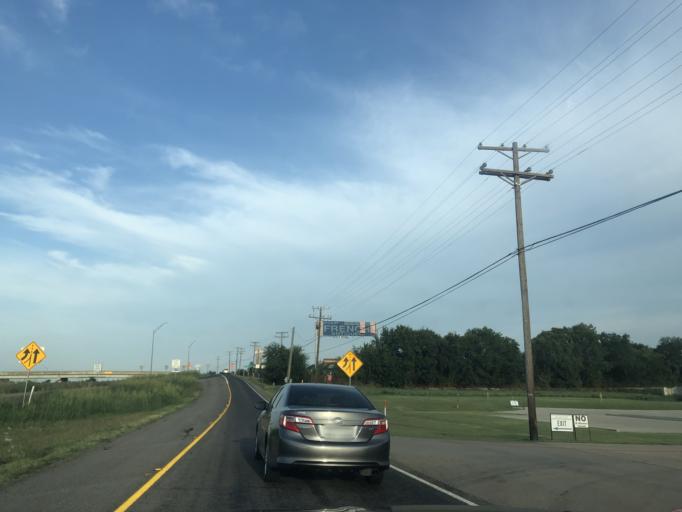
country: US
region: Texas
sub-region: Dallas County
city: Sunnyvale
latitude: 32.7807
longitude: -96.5392
